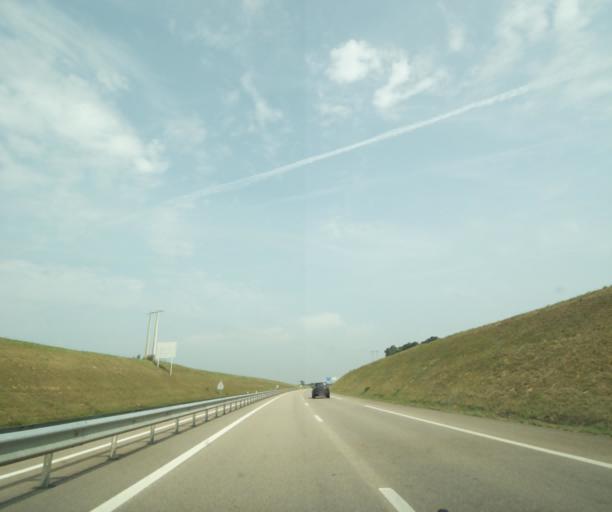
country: FR
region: Lower Normandy
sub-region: Departement du Calvados
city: Falaise
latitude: 48.8799
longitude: -0.2196
